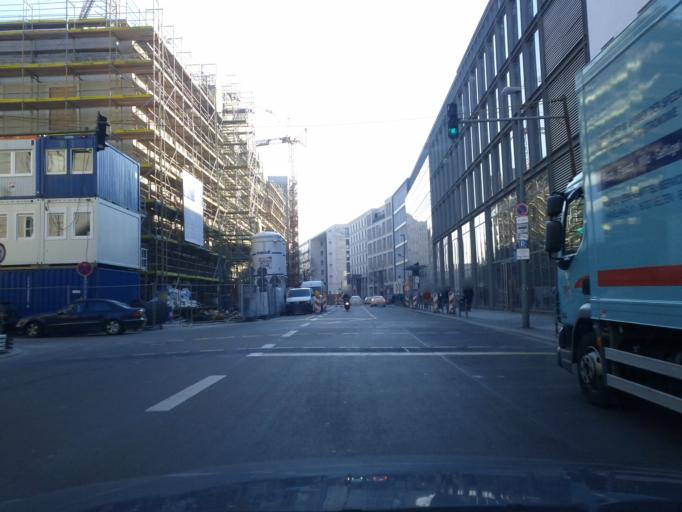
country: DE
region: Berlin
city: Mitte
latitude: 52.5151
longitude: 13.3951
